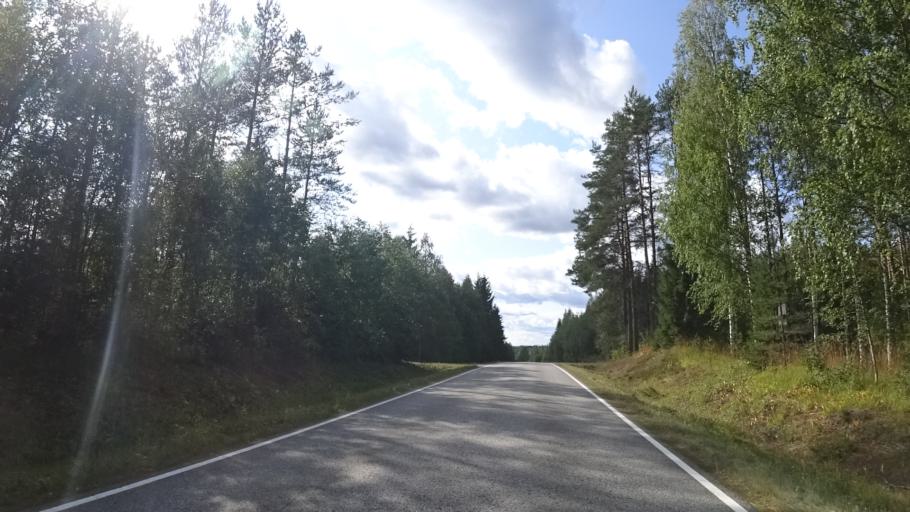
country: RU
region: Republic of Karelia
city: Vyartsilya
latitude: 62.2692
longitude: 30.7954
